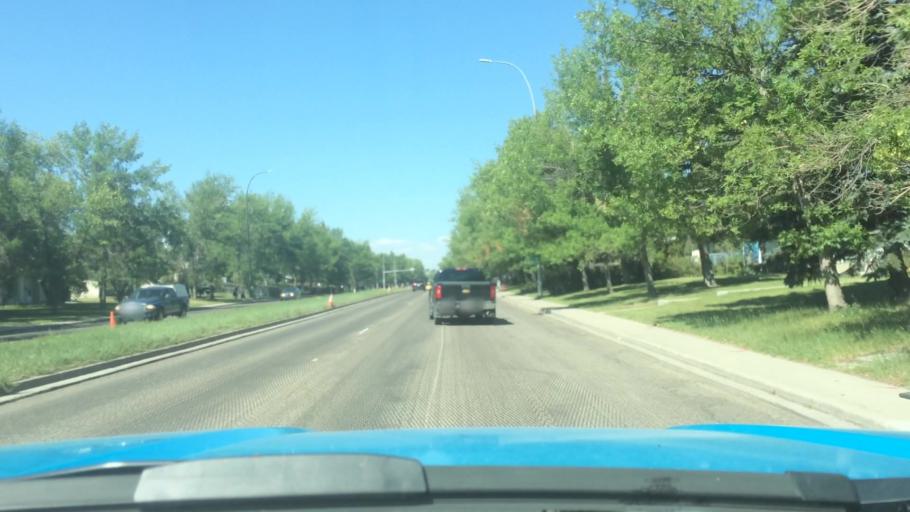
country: CA
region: Alberta
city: Calgary
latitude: 51.0529
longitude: -113.9595
